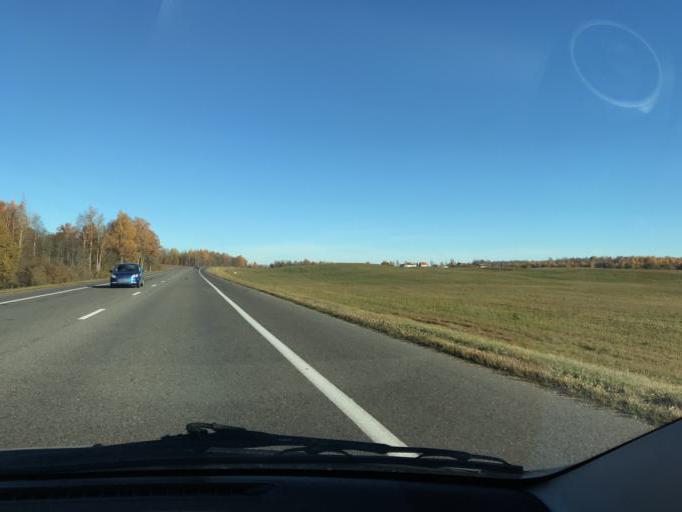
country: BY
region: Vitebsk
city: Vitebsk
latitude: 55.0709
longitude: 30.3087
